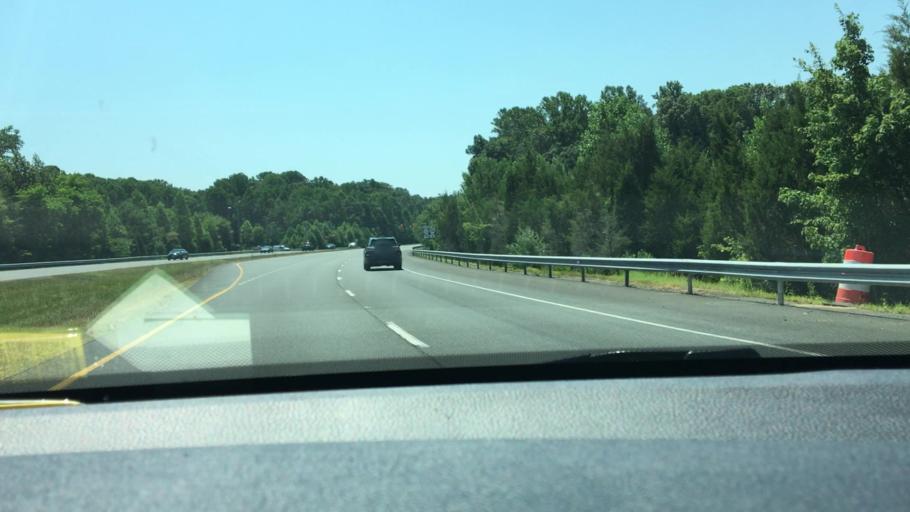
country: US
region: Virginia
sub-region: Prince William County
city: Buckhall
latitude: 38.7320
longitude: -77.4251
